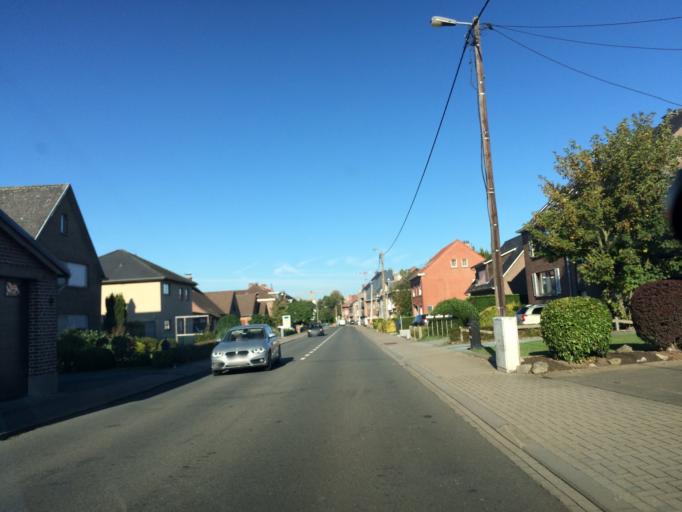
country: BE
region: Flanders
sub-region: Provincie Vlaams-Brabant
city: Merchtem
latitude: 50.9549
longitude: 4.2388
